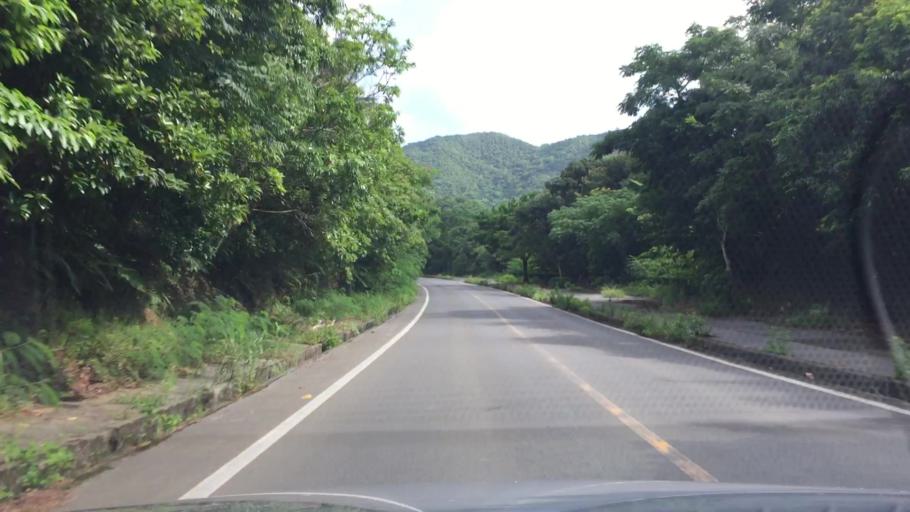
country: JP
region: Okinawa
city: Ishigaki
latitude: 24.4287
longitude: 124.2107
